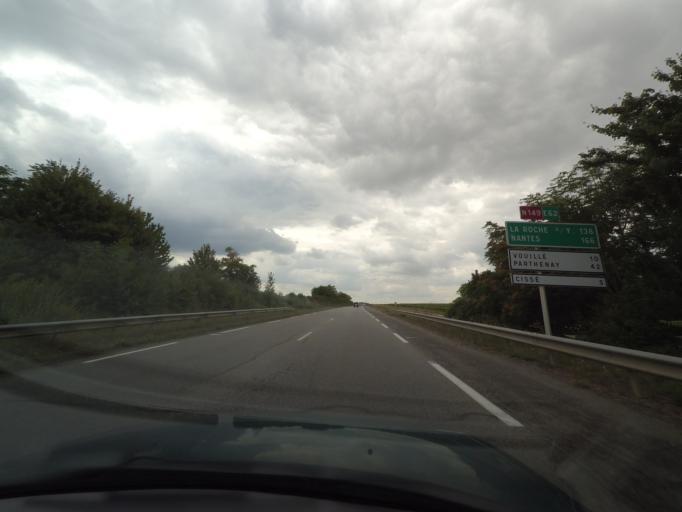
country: FR
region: Poitou-Charentes
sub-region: Departement de la Vienne
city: Migne-Auxances
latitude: 46.6318
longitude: 0.2767
